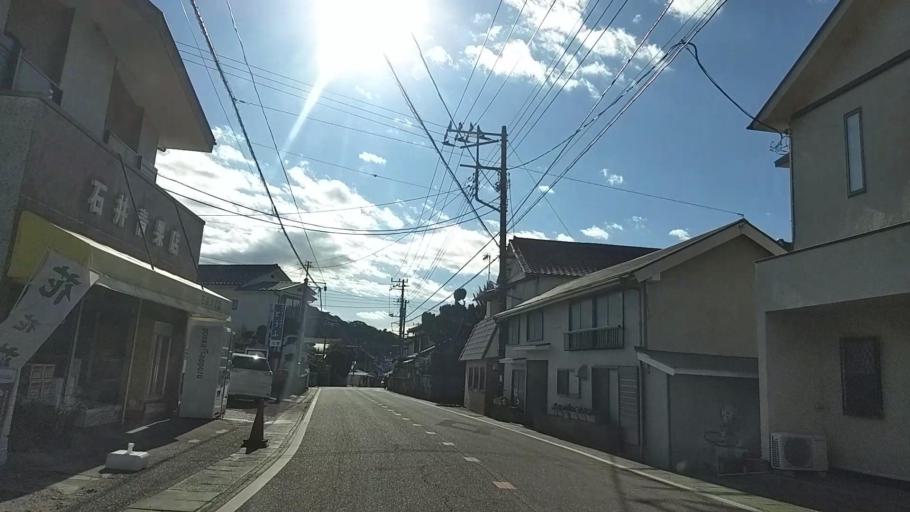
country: JP
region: Chiba
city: Tateyama
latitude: 35.0614
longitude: 139.8273
